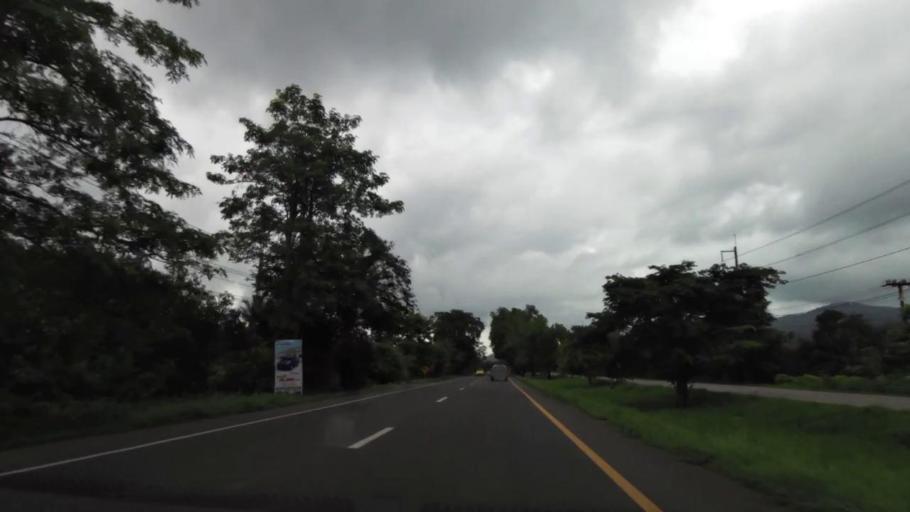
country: TH
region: Chanthaburi
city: Tha Mai
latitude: 12.6781
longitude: 102.0053
